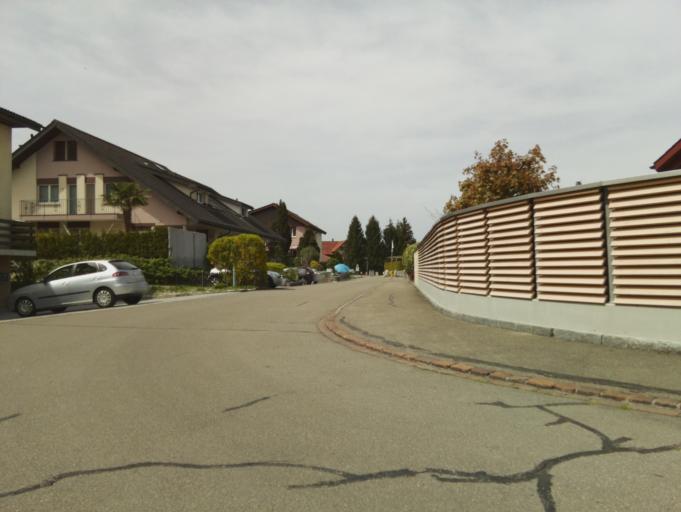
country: CH
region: Schwyz
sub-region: Bezirk March
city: Lachen
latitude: 47.1759
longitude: 8.8891
